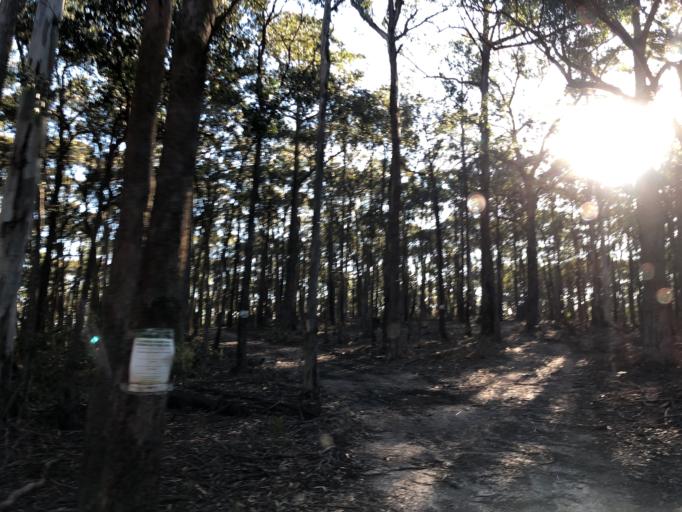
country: AU
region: Victoria
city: Brown Hill
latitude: -37.5079
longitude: 144.1845
